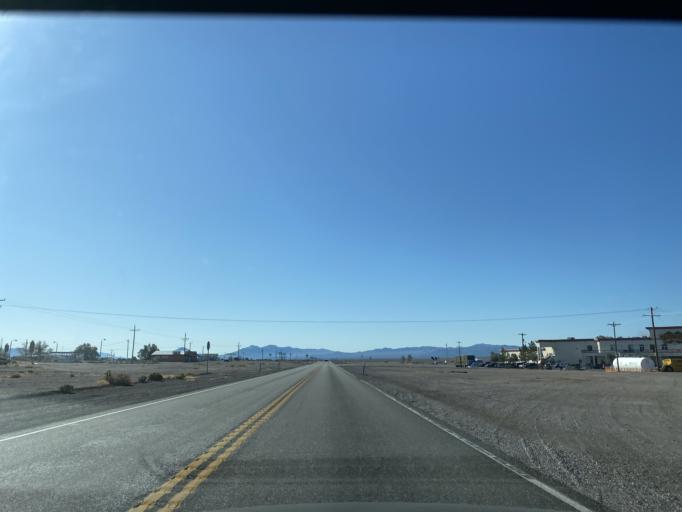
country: US
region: Nevada
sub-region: Nye County
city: Pahrump
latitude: 36.4148
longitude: -116.4223
